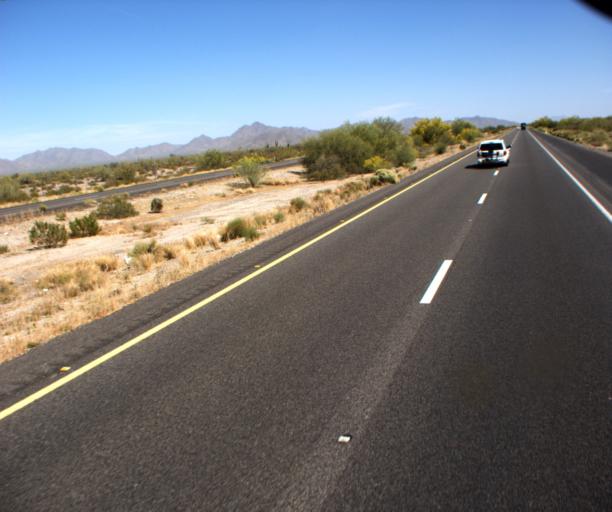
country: US
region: Arizona
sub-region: Maricopa County
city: Gila Bend
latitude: 32.9048
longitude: -112.5280
